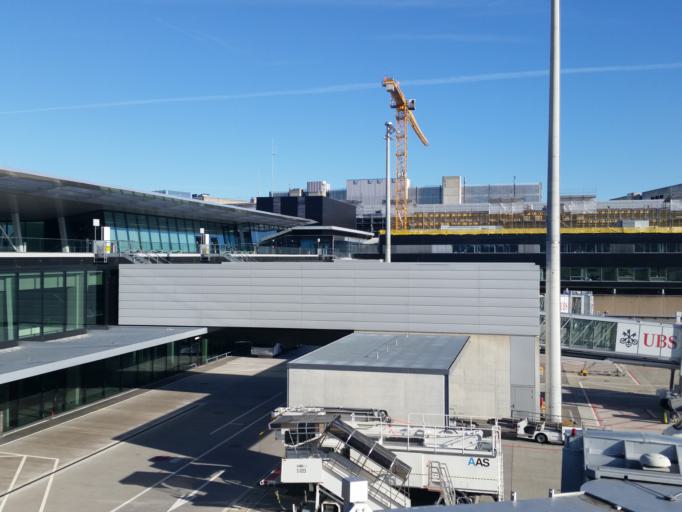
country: CH
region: Zurich
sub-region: Bezirk Buelach
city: Glattbrugg / Rohr/Platten-Balsberg
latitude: 47.4506
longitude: 8.5583
